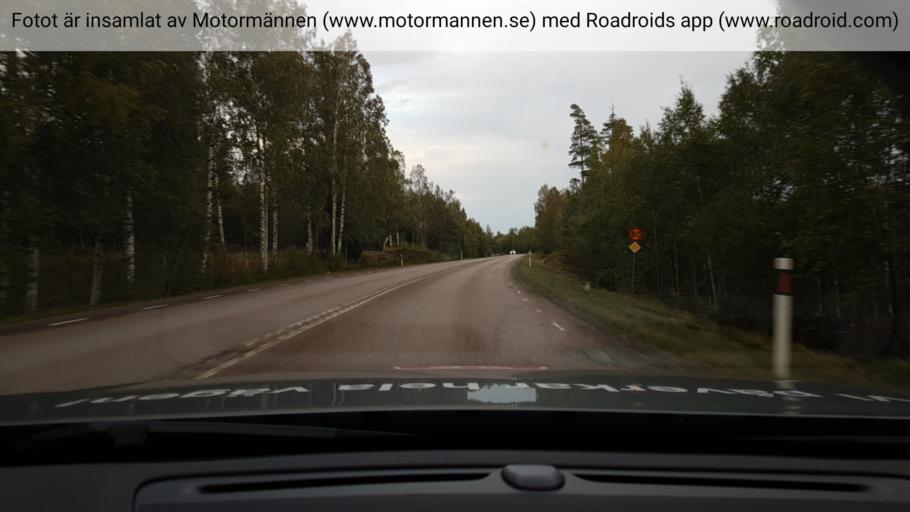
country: SE
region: Vaestra Goetaland
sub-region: Amals Kommun
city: Amal
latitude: 59.0747
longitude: 12.5716
